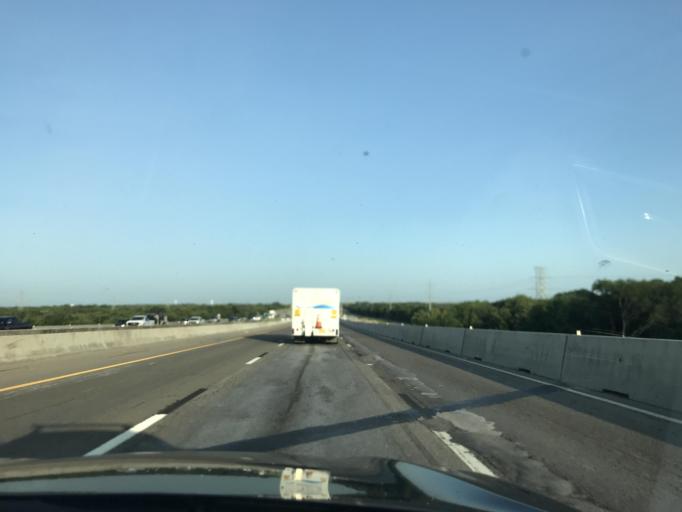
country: US
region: Texas
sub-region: Tarrant County
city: Benbrook
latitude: 32.6835
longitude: -97.4244
